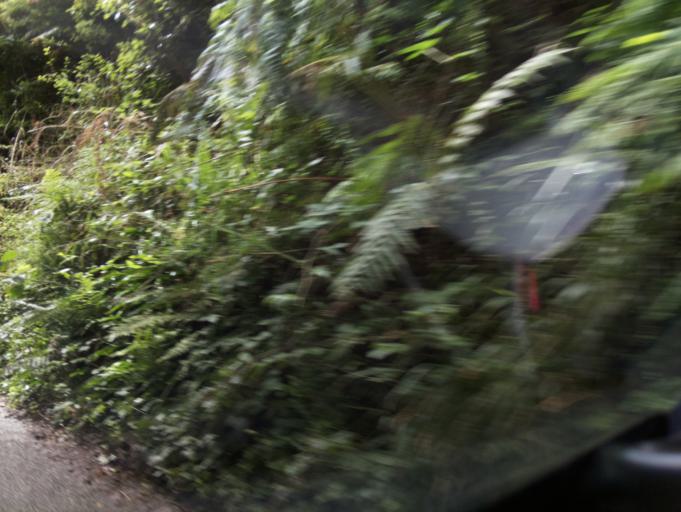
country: GB
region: England
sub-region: Devon
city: Kingsbridge
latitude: 50.2879
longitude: -3.7174
